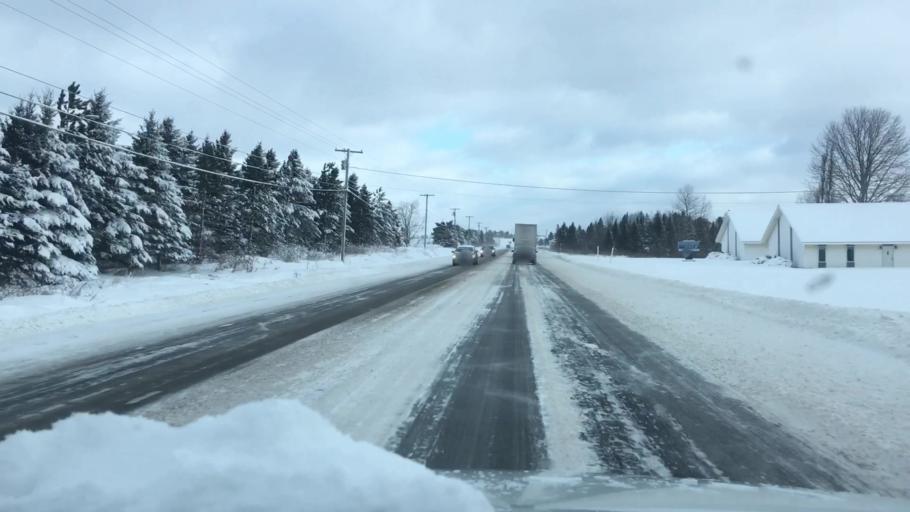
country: US
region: Maine
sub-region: Aroostook County
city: Presque Isle
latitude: 46.7357
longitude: -67.9995
